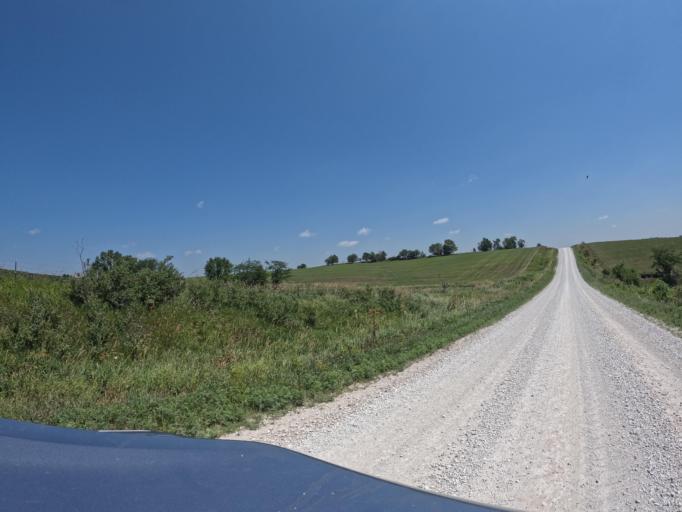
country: US
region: Iowa
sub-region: Keokuk County
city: Sigourney
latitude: 41.2579
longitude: -92.1577
